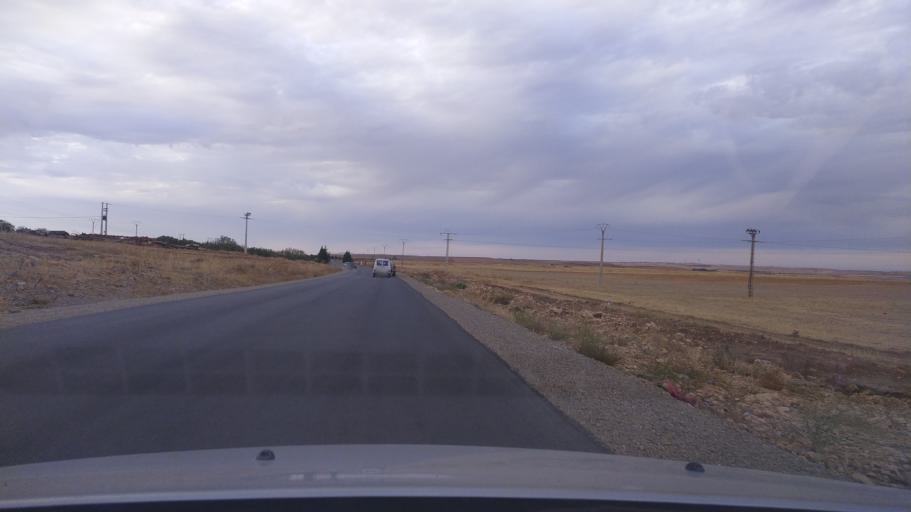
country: DZ
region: Tiaret
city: Frenda
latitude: 35.0106
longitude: 1.1173
